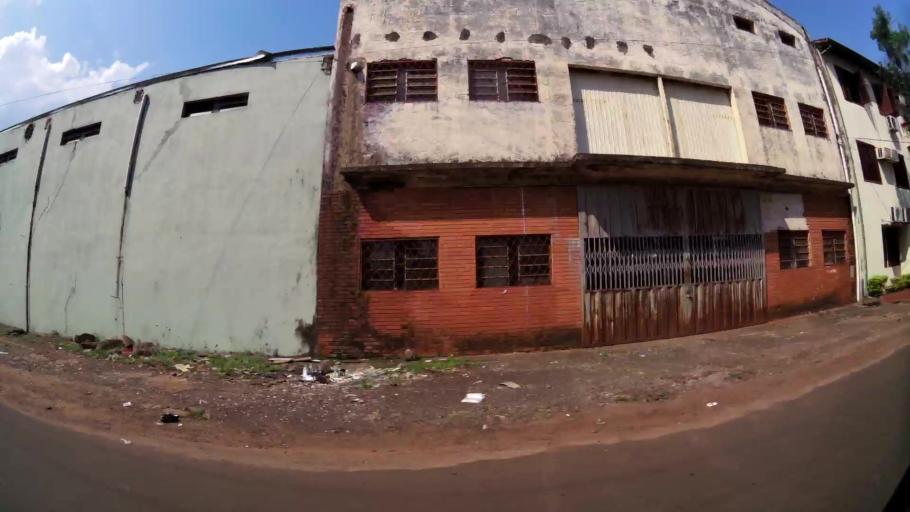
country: PY
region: Alto Parana
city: Ciudad del Este
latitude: -25.5077
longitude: -54.6208
